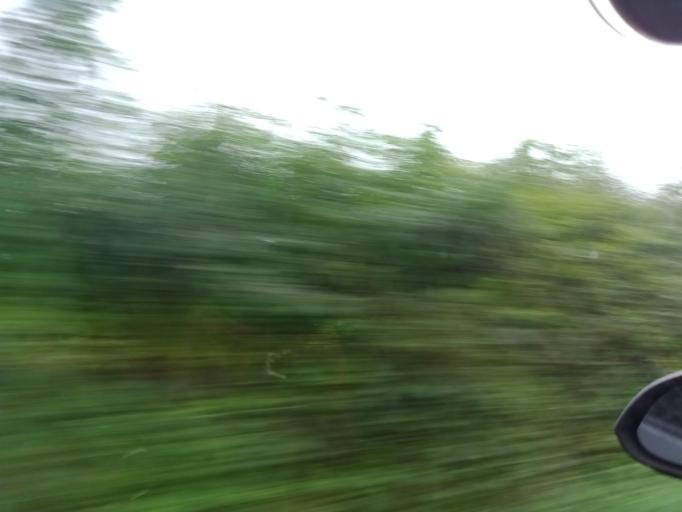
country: IE
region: Leinster
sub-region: Kilkenny
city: Castlecomer
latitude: 52.8504
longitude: -7.1756
